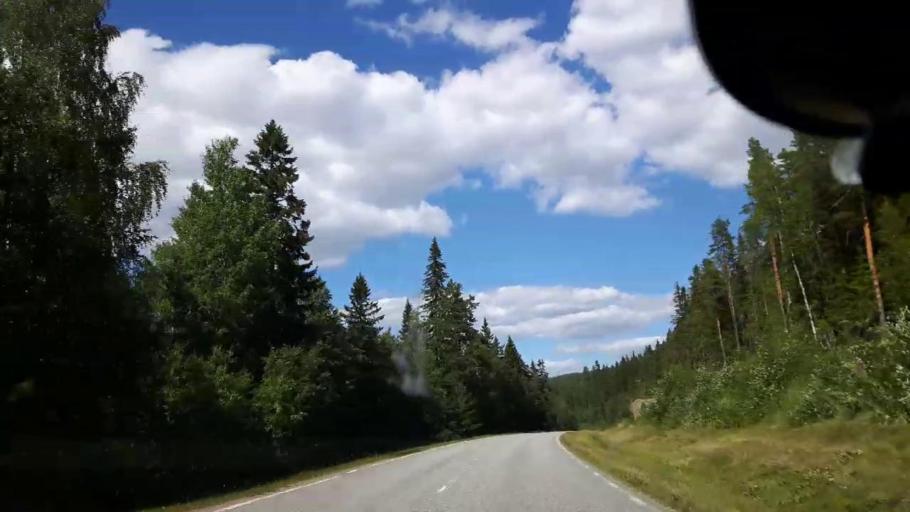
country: SE
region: Vaesternorrland
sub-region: Ange Kommun
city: Fransta
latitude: 62.7224
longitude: 16.3308
